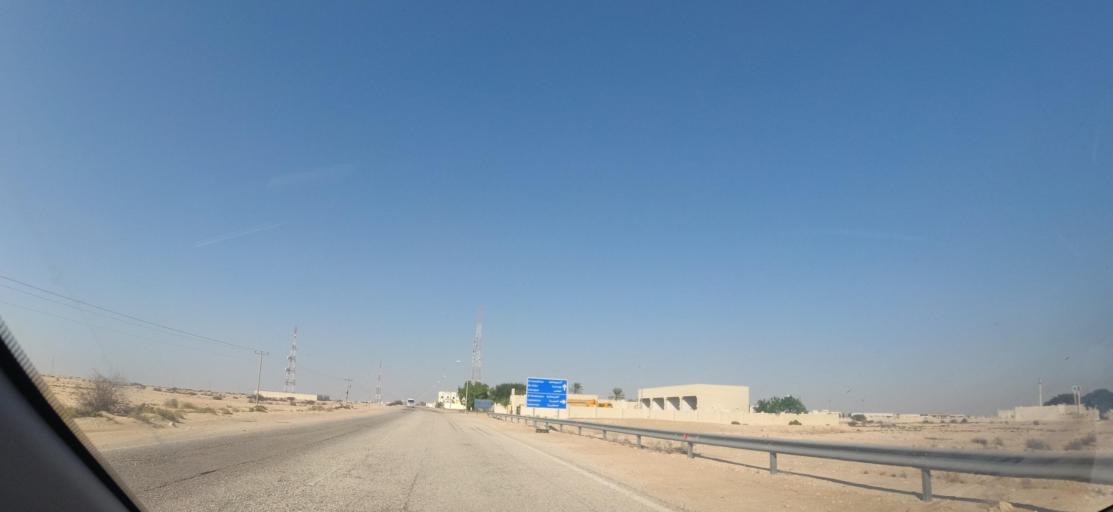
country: QA
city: Al Jumayliyah
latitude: 25.6156
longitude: 51.0789
